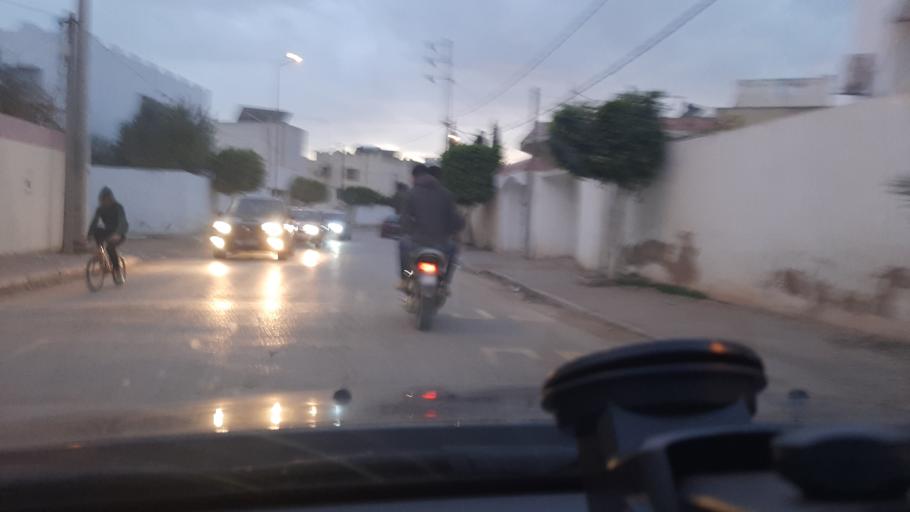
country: TN
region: Safaqis
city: Sfax
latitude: 34.7679
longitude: 10.7022
